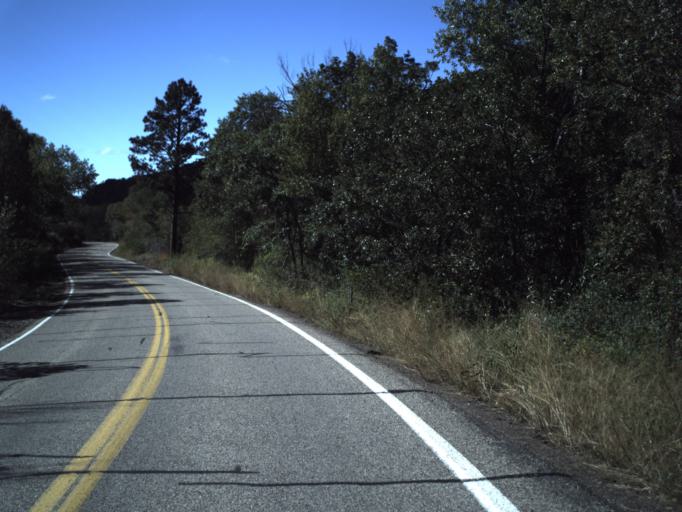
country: US
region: Utah
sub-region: Beaver County
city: Beaver
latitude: 38.2792
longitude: -112.5642
